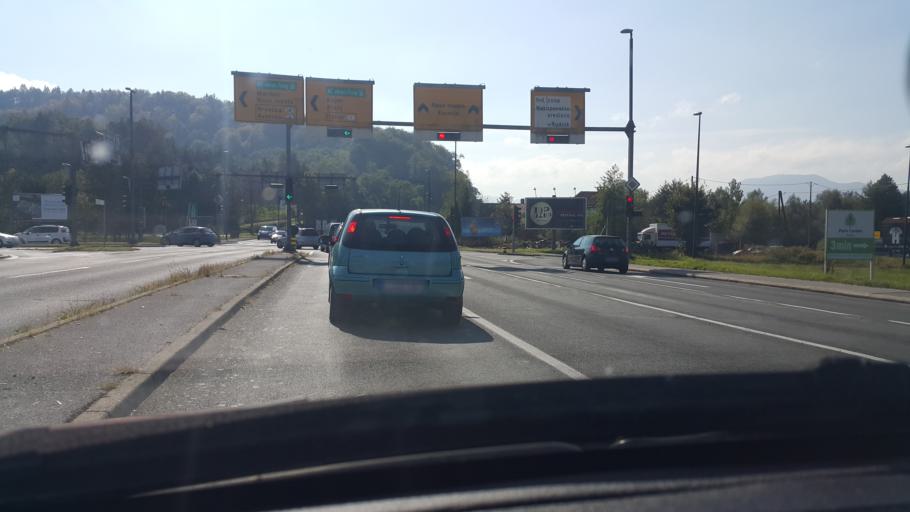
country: SI
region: Skofljica
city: Lavrica
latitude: 46.0169
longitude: 14.5433
